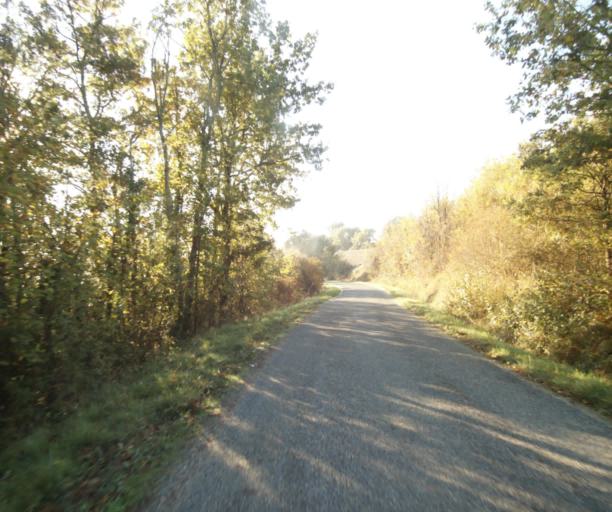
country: FR
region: Midi-Pyrenees
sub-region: Departement de la Haute-Garonne
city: Villemur-sur-Tarn
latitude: 43.8920
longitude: 1.4857
